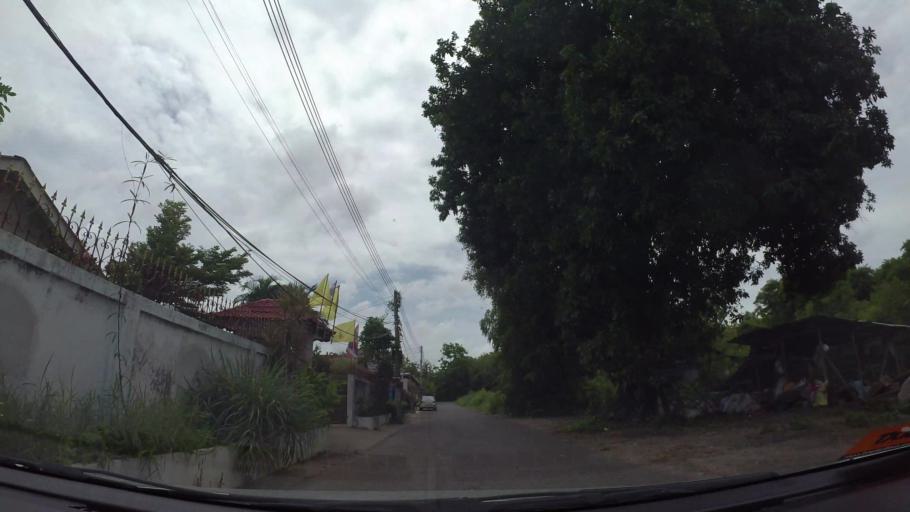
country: TH
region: Chon Buri
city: Sattahip
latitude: 12.6784
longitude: 100.9083
